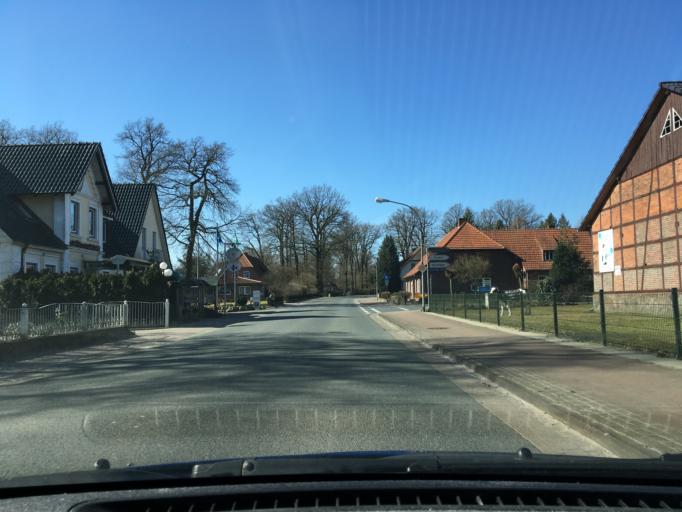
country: DE
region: Lower Saxony
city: Neuenkirchen
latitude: 53.0667
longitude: 9.6654
